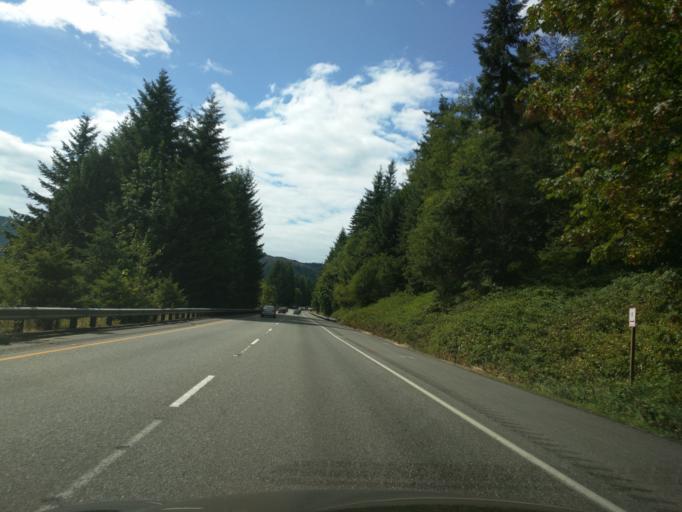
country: US
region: Washington
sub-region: Whatcom County
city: Sudden Valley
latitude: 48.6686
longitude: -122.3760
